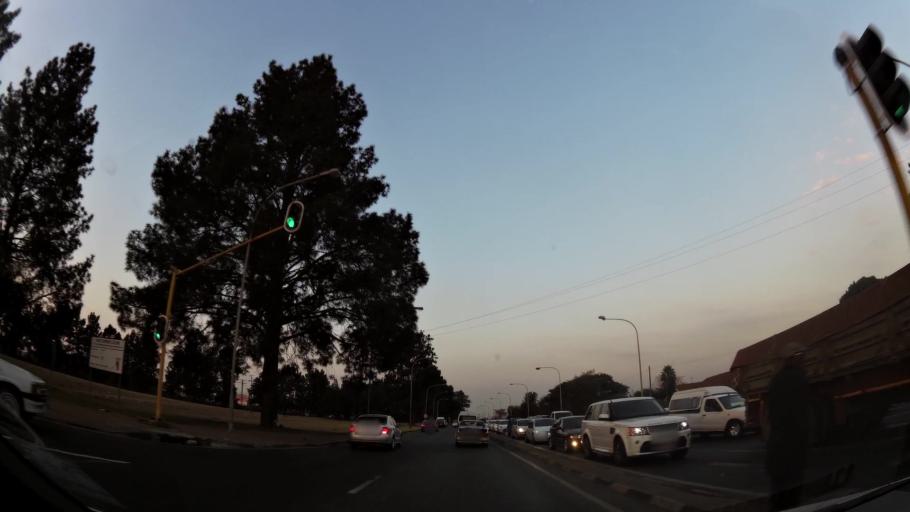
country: ZA
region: Gauteng
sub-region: Ekurhuleni Metropolitan Municipality
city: Springs
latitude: -26.2665
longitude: 28.4177
